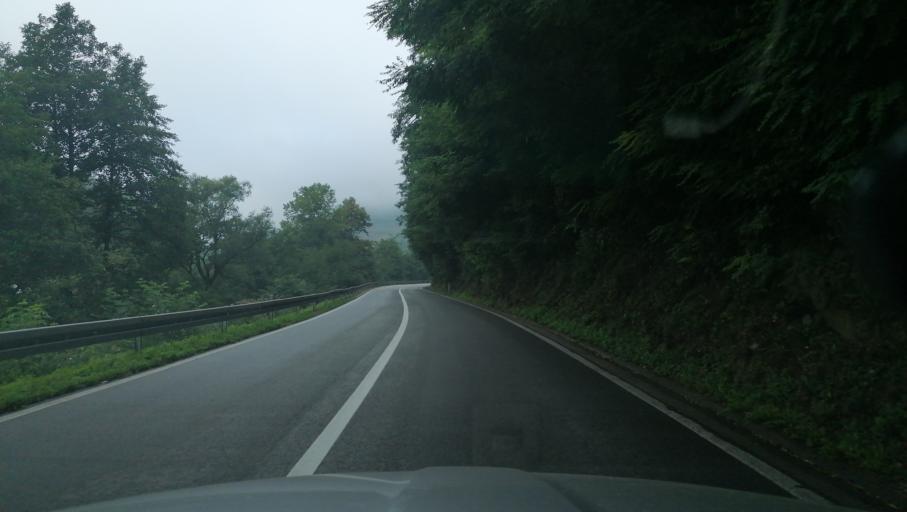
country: BA
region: Federation of Bosnia and Herzegovina
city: Donji Vakuf
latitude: 44.1678
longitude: 17.3604
